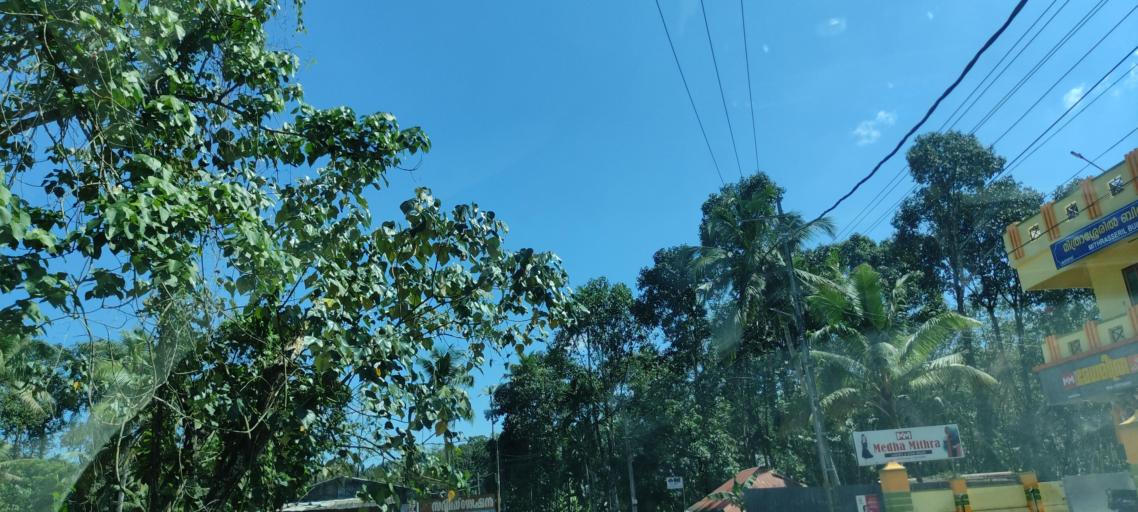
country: IN
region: Kerala
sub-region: Pattanamtitta
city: Adur
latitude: 9.0908
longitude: 76.6901
